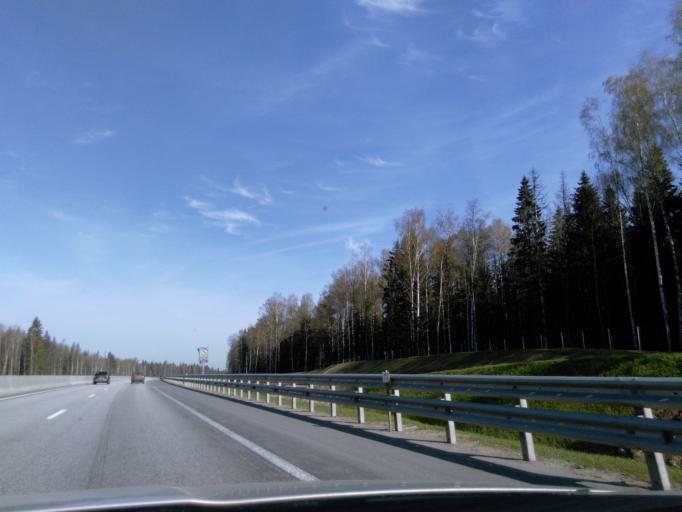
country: RU
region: Moskovskaya
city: Mendeleyevo
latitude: 56.0697
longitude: 37.2228
